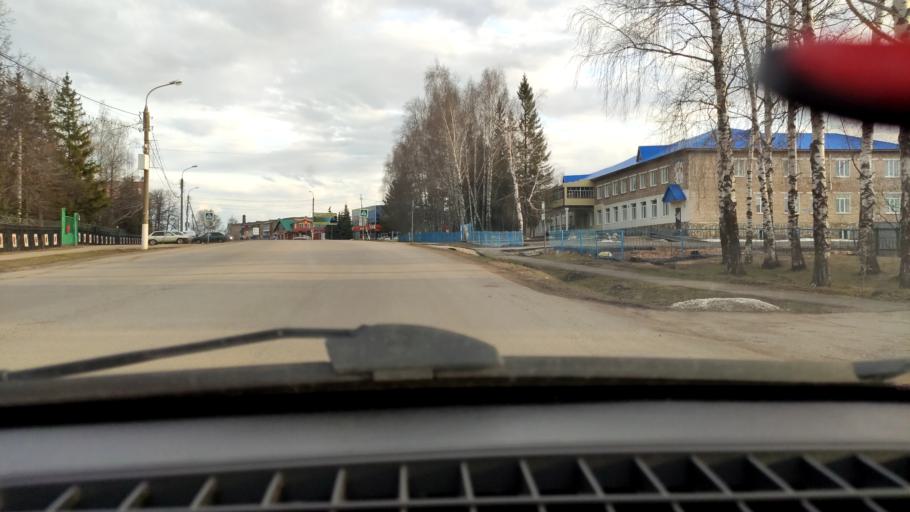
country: RU
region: Bashkortostan
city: Tolbazy
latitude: 54.0124
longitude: 55.8864
